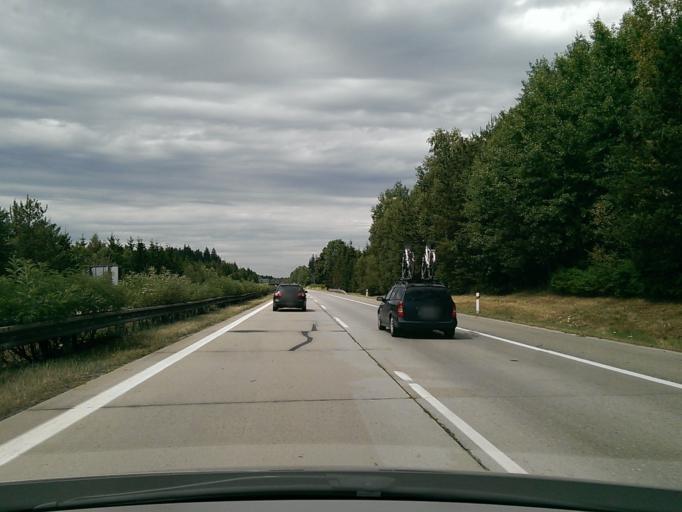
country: CZ
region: Vysocina
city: Luka nad Jihlavou
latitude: 49.4108
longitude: 15.7366
